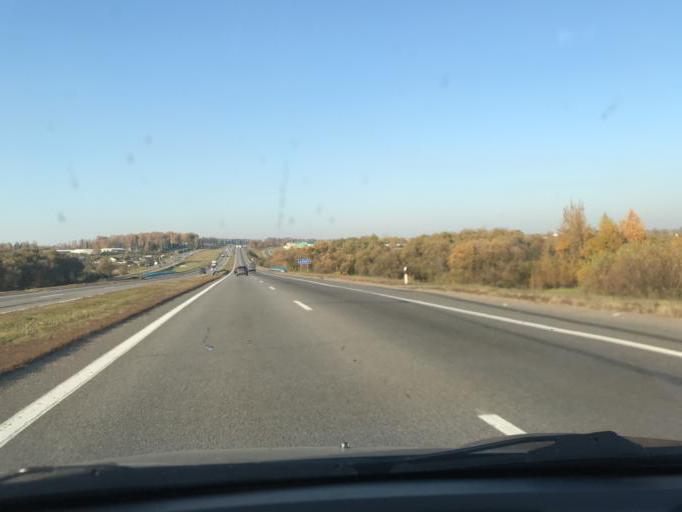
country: BY
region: Minsk
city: Samakhvalavichy
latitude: 53.7398
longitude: 27.5158
